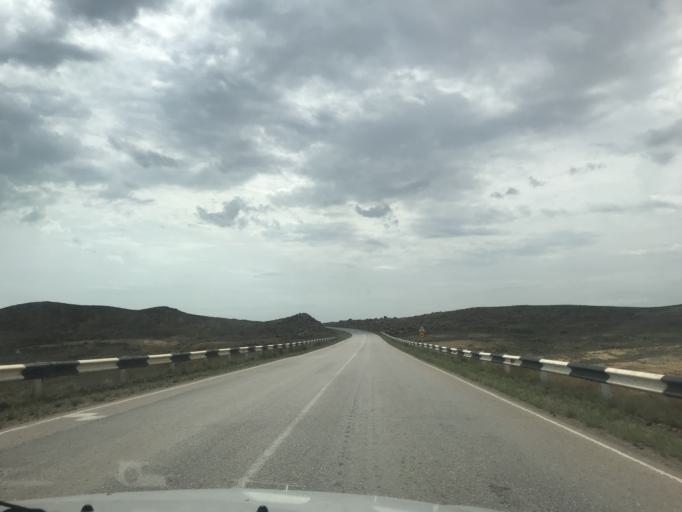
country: KZ
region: Zhambyl
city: Mynaral
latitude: 45.5113
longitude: 73.4973
